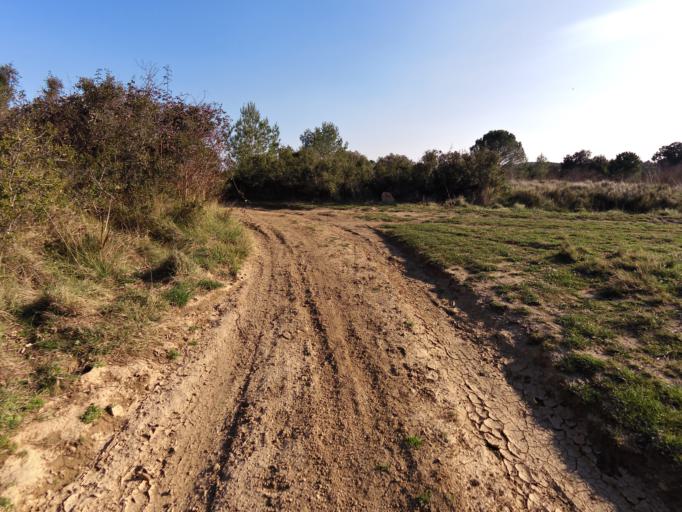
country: FR
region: Languedoc-Roussillon
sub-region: Departement du Gard
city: Congenies
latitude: 43.7563
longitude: 4.1781
